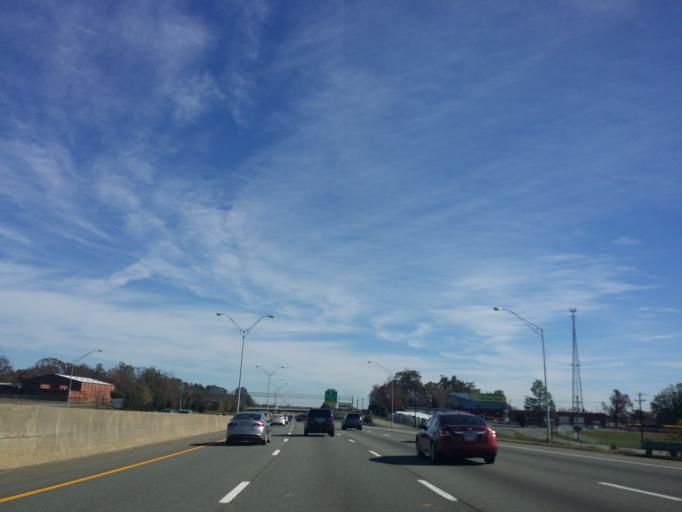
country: US
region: North Carolina
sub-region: Alamance County
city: Graham
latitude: 36.0600
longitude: -79.3975
